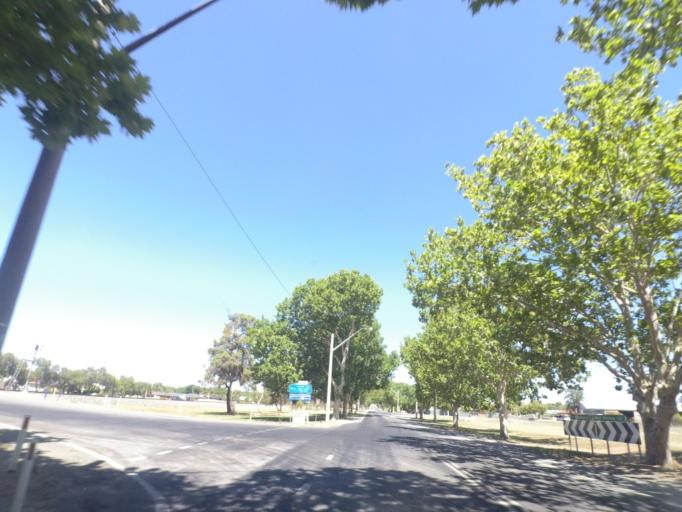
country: AU
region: New South Wales
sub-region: Narrandera
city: Narrandera
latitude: -34.7394
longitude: 146.5674
